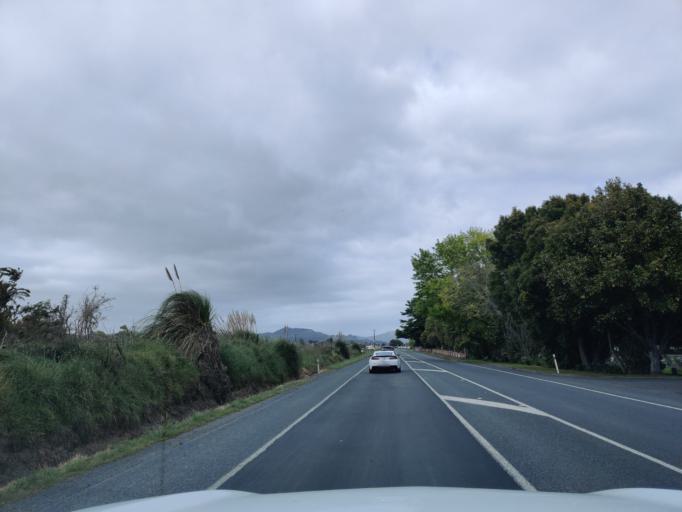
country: NZ
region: Waikato
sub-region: Waikato District
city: Te Kauwhata
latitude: -37.5304
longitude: 175.1592
